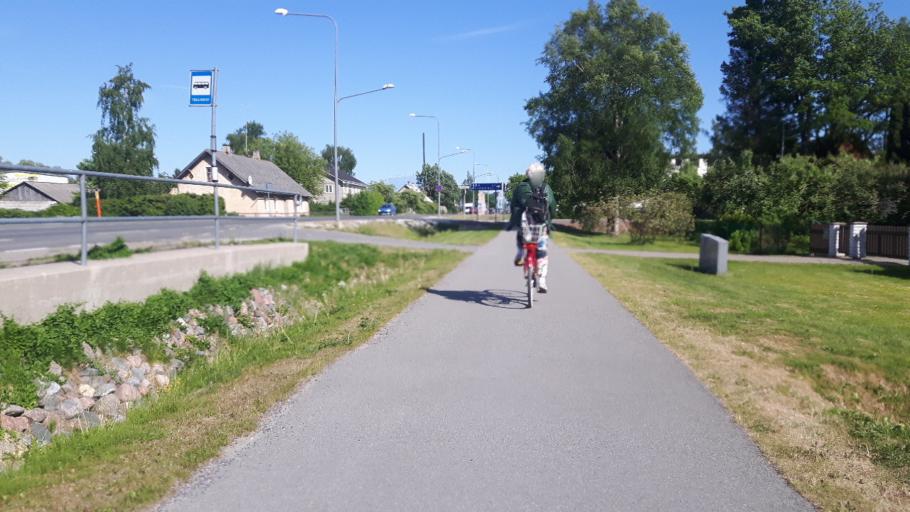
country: EE
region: Raplamaa
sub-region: Rapla vald
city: Rapla
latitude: 58.9932
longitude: 24.8253
